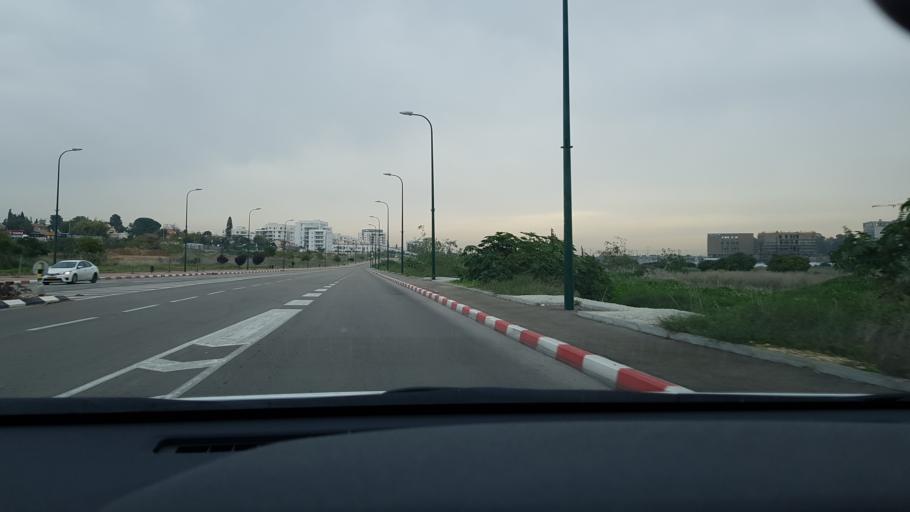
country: IL
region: Central District
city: Ness Ziona
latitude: 31.9206
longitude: 34.7993
